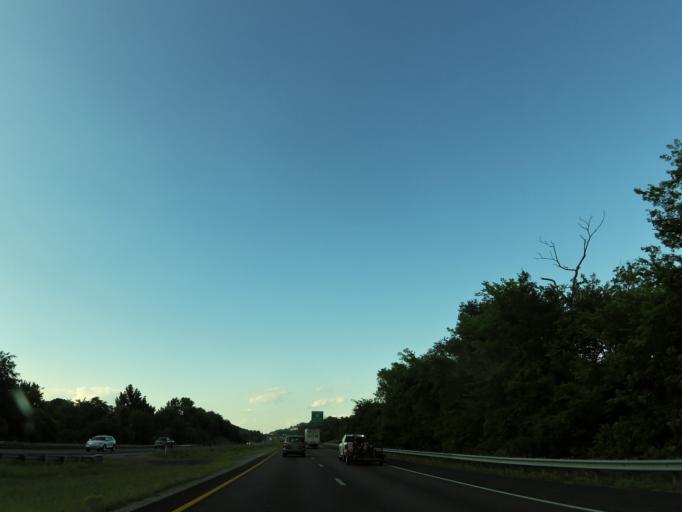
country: US
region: Tennessee
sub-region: Williamson County
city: Thompson's Station
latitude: 35.8060
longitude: -86.8498
